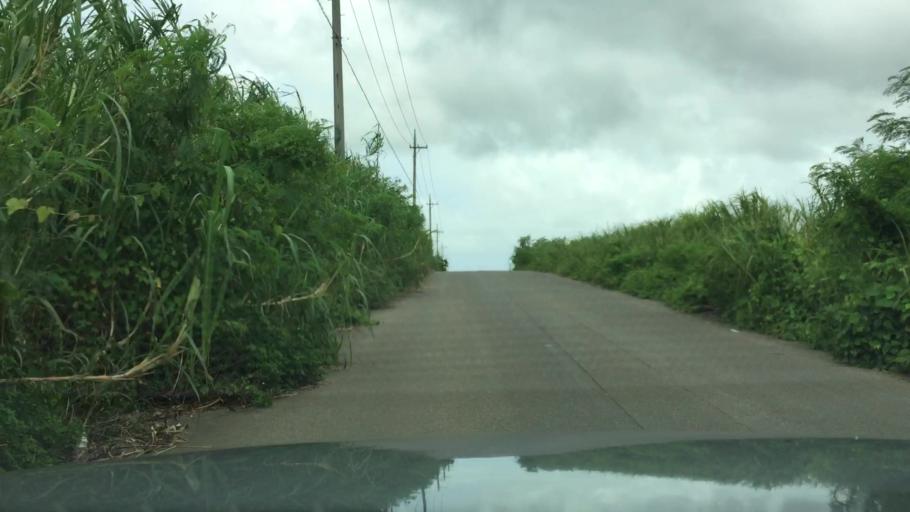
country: JP
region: Okinawa
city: Ishigaki
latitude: 24.3974
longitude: 124.1916
